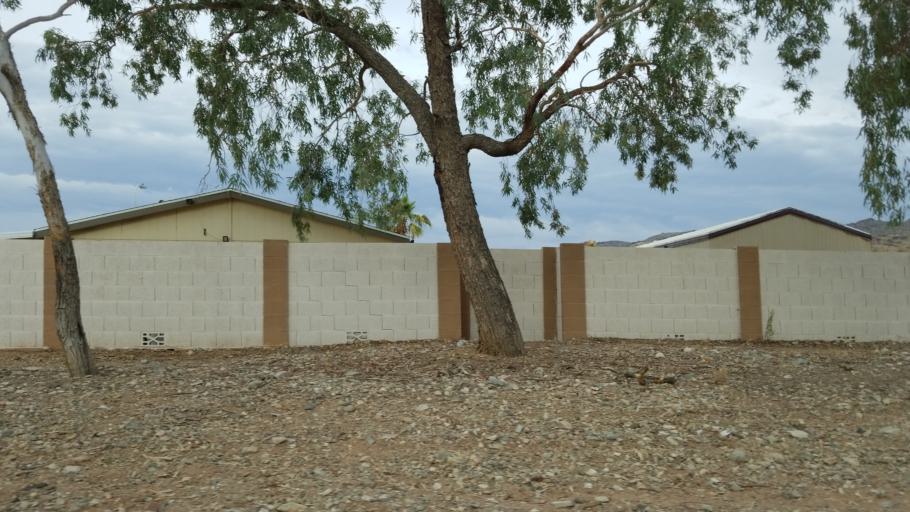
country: US
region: Arizona
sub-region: Maricopa County
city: Laveen
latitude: 33.3560
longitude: -112.0920
